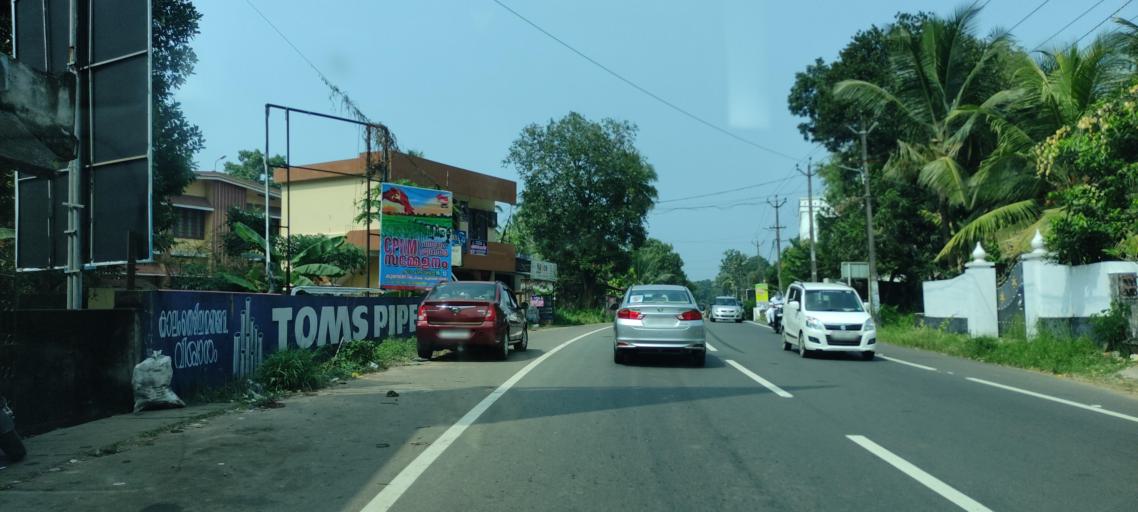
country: IN
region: Kerala
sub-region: Pattanamtitta
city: Adur
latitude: 9.2002
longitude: 76.6943
